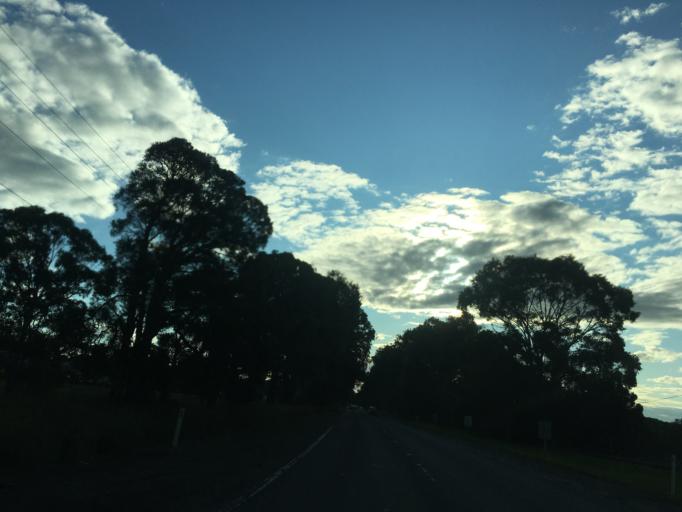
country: AU
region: New South Wales
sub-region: Fairfield
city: Cecil Park
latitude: -33.8775
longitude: 150.7809
